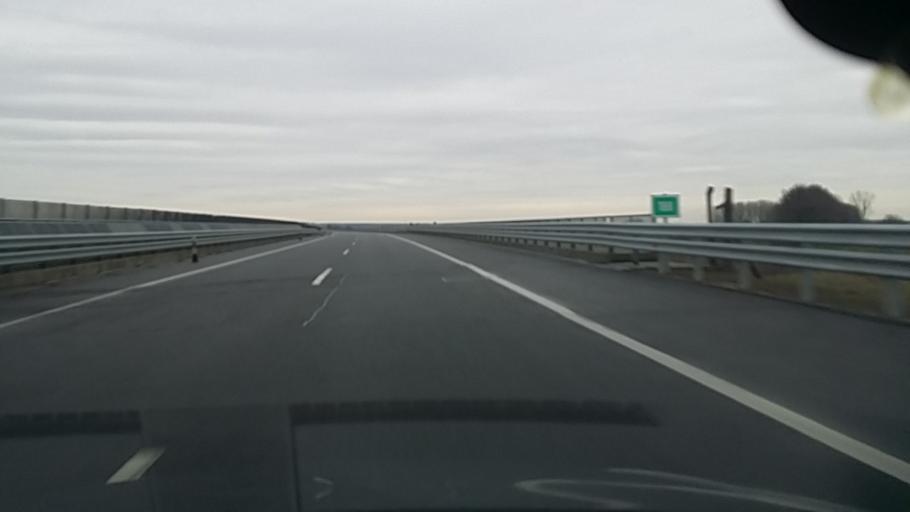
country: HU
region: Hajdu-Bihar
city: Gorbehaza
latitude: 47.7943
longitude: 21.2709
